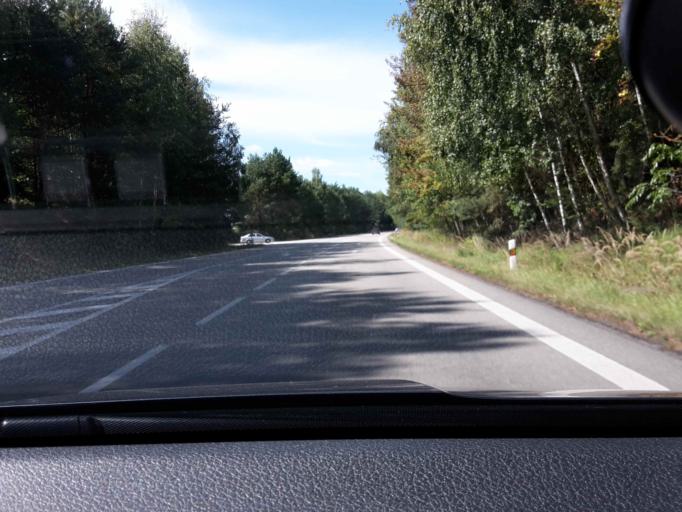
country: CZ
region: Jihocesky
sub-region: Okres Jindrichuv Hradec
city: Jindrichuv Hradec
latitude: 49.1537
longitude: 14.9879
